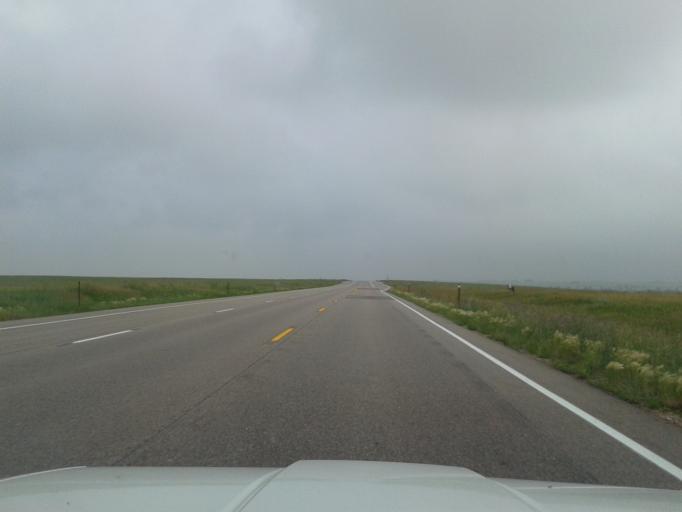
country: US
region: Colorado
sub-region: Elbert County
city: Ponderosa Park
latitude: 39.3094
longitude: -104.7354
